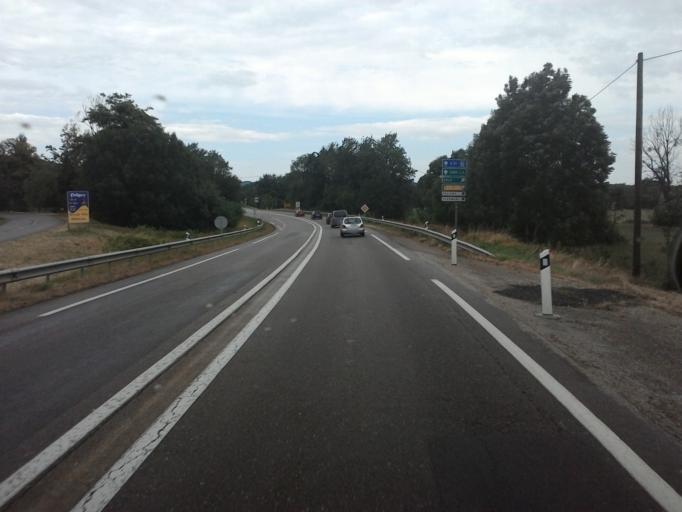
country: FR
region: Franche-Comte
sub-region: Departement du Jura
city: Poligny
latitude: 46.8483
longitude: 5.7055
